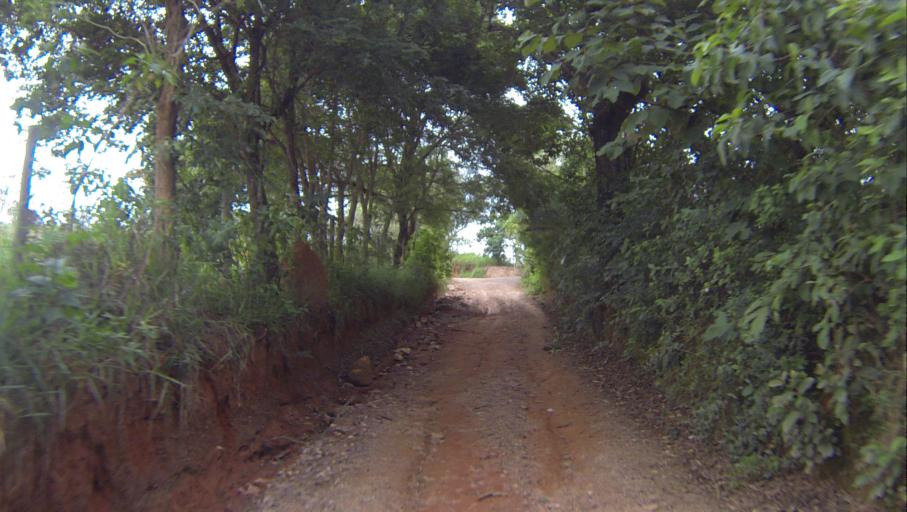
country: BR
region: Minas Gerais
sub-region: Brumadinho
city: Brumadinho
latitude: -20.1614
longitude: -44.1311
